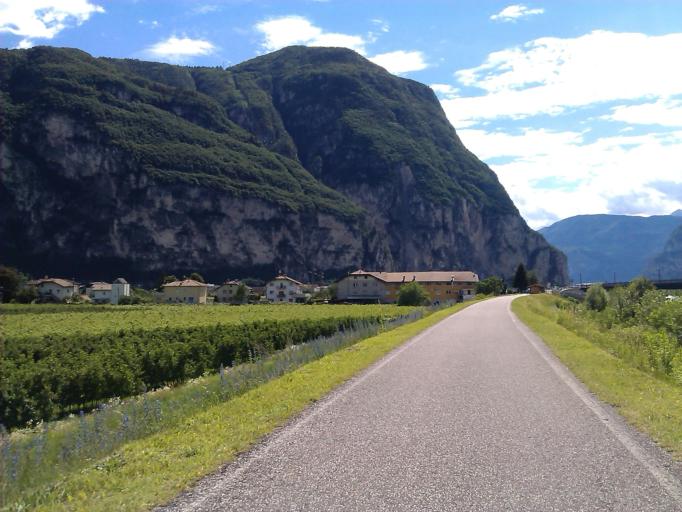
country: IT
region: Trentino-Alto Adige
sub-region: Bolzano
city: Salorno
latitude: 46.2451
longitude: 11.2083
